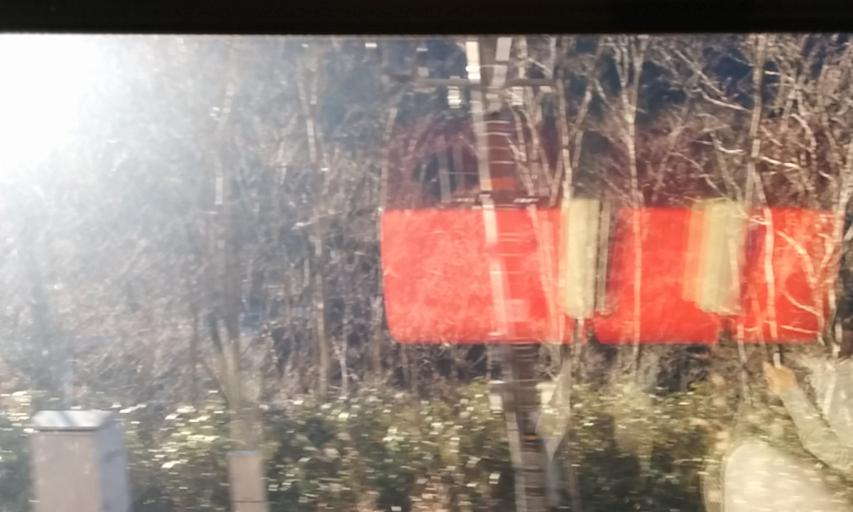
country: JP
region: Nagano
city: Ina
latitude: 35.7941
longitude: 137.6884
